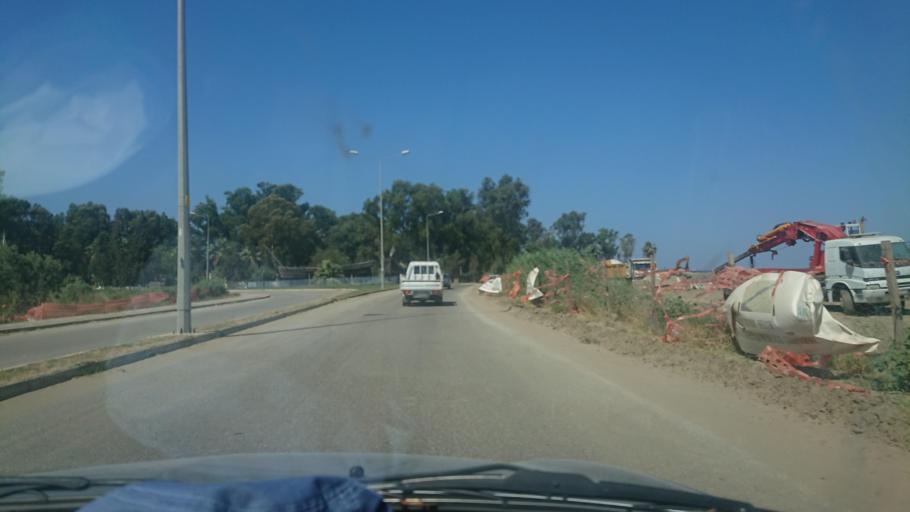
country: TR
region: Aydin
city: Kusadasi
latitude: 37.9413
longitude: 27.2780
